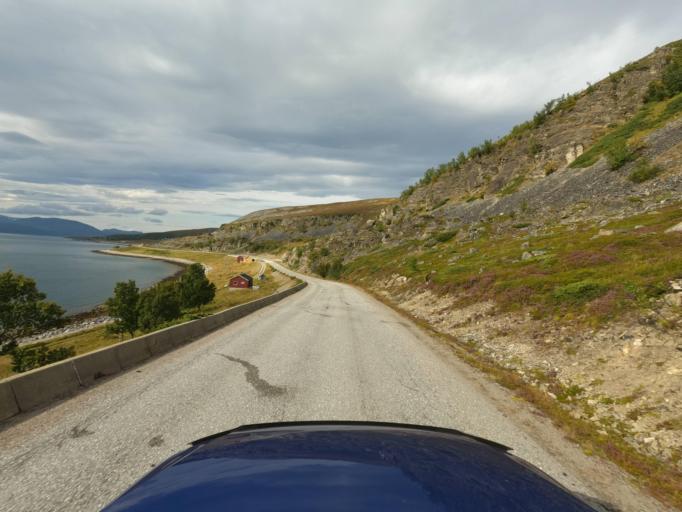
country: NO
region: Finnmark Fylke
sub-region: Kvalsund
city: Kvalsund
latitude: 70.5075
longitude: 23.8832
